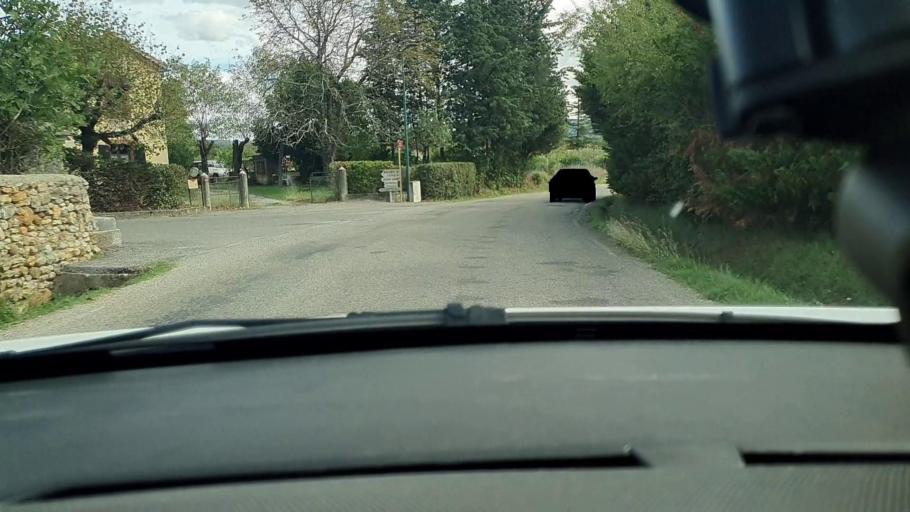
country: FR
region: Languedoc-Roussillon
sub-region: Departement du Gard
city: Les Mages
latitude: 44.2108
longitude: 4.1989
